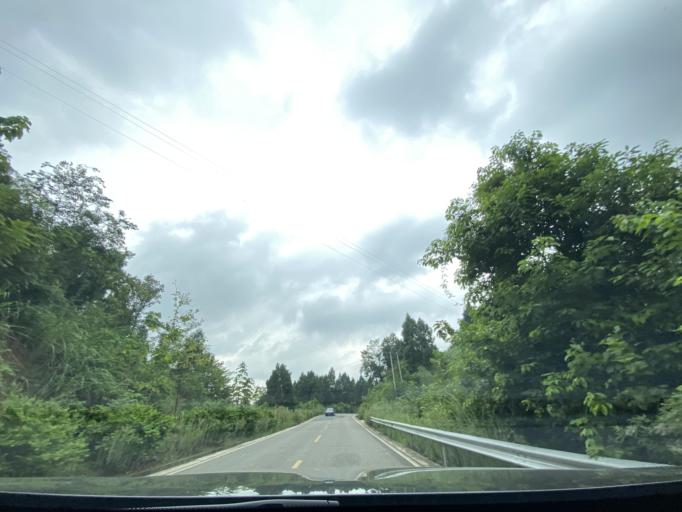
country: CN
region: Sichuan
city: Jiancheng
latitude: 30.5358
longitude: 104.5312
